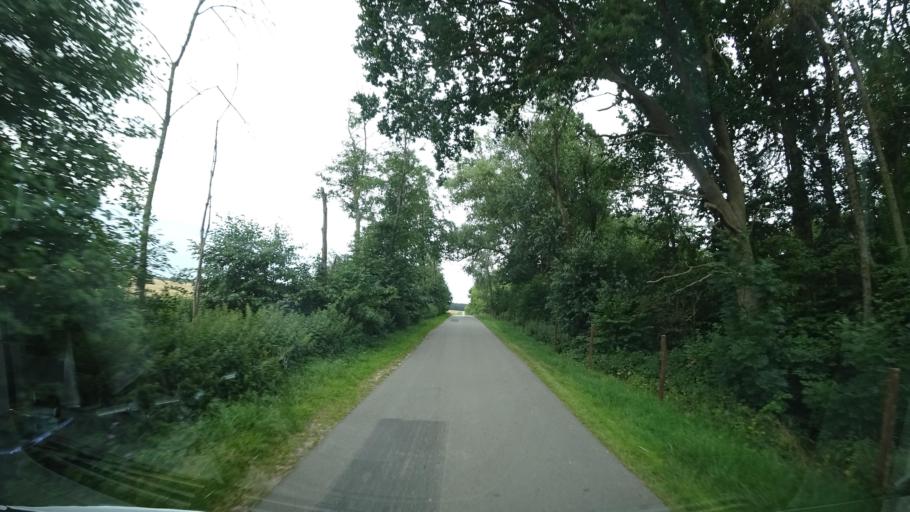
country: DE
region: Mecklenburg-Vorpommern
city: Rambin
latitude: 54.3218
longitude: 13.2022
